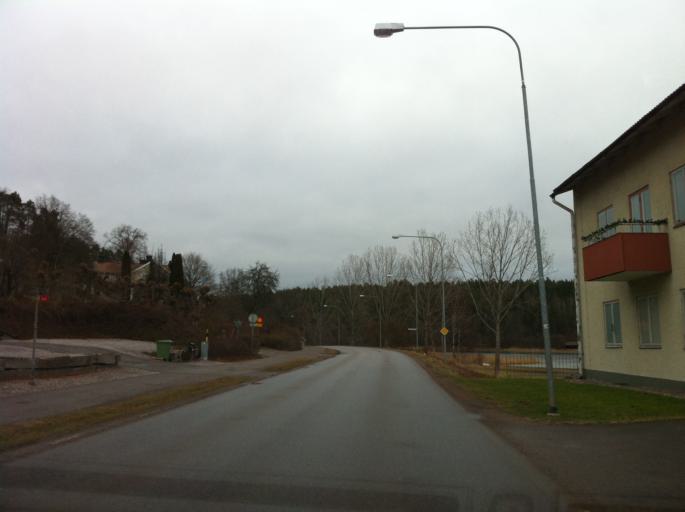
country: SE
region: Kalmar
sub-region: Vasterviks Kommun
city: Overum
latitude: 57.9013
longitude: 16.0532
